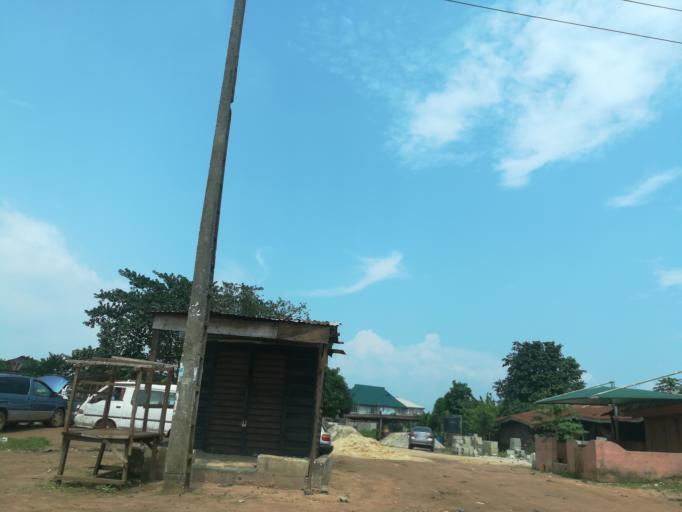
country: NG
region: Lagos
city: Ikorodu
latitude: 6.5877
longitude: 3.6246
